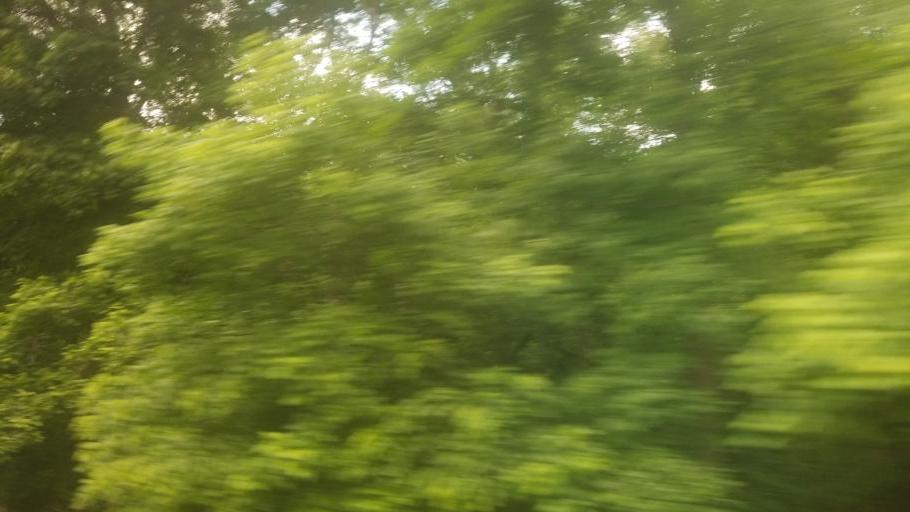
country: US
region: Maryland
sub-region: Frederick County
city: Brunswick
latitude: 39.3073
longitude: -77.5875
